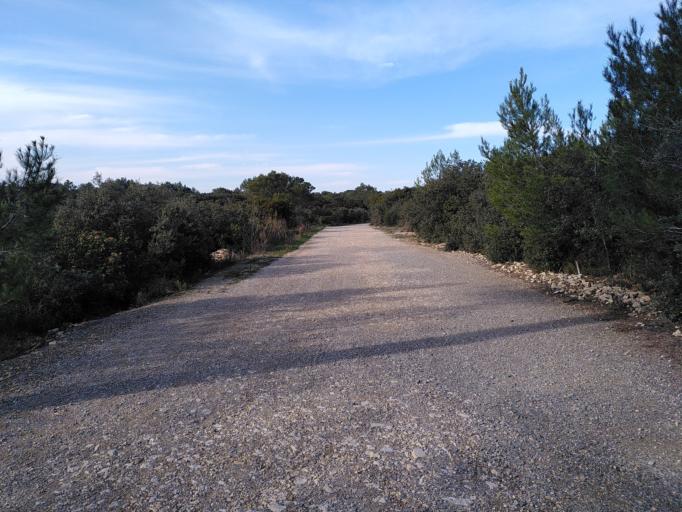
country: FR
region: Languedoc-Roussillon
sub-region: Departement du Gard
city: Caveirac
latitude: 43.8340
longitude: 4.2931
